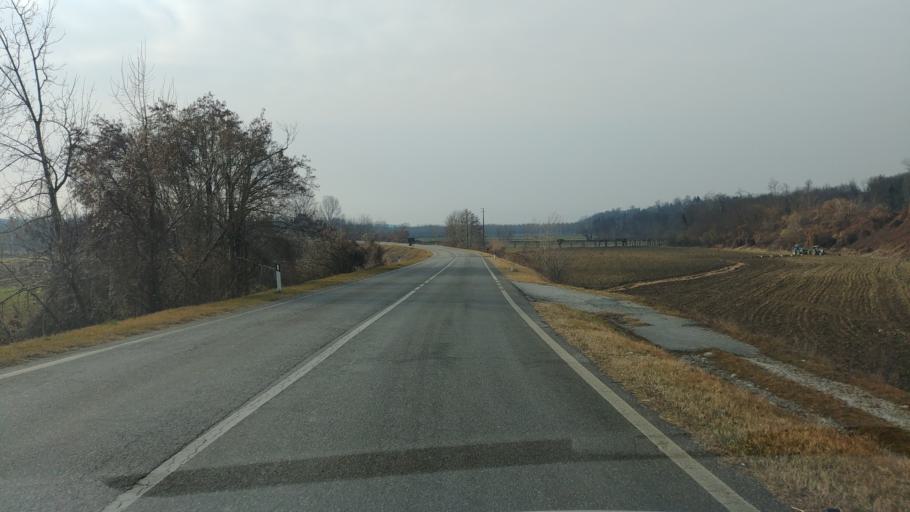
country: IT
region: Piedmont
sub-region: Provincia di Cuneo
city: Castelletto Stura
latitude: 44.4586
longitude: 7.6358
